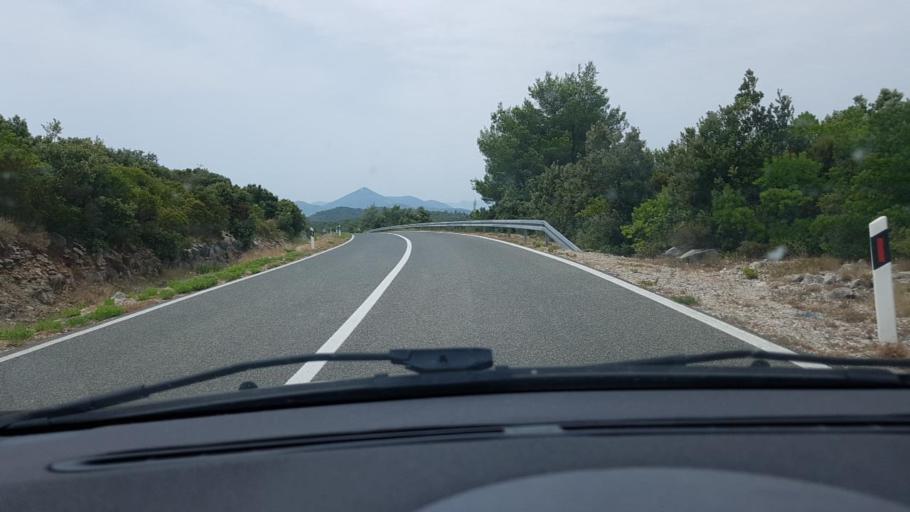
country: HR
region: Dubrovacko-Neretvanska
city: Smokvica
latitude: 42.9494
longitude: 16.9494
